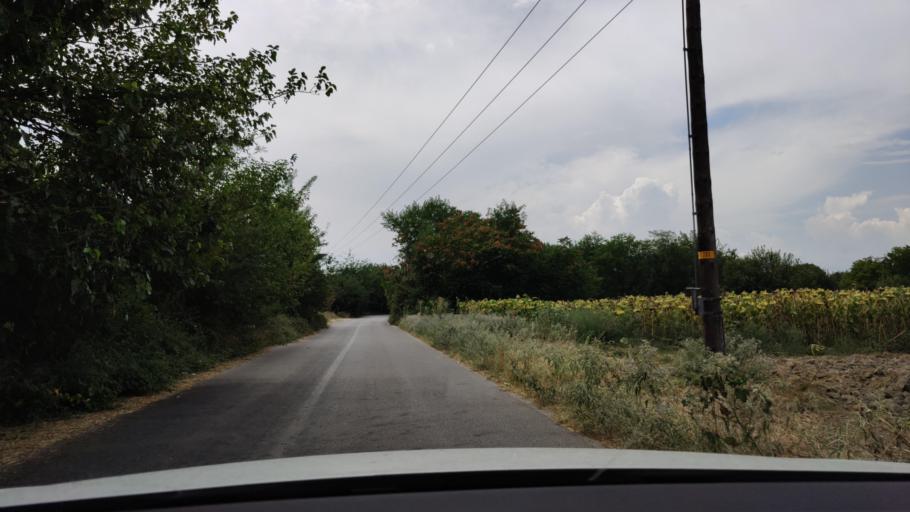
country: GR
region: Central Macedonia
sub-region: Nomos Serron
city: Serres
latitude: 41.0692
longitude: 23.5593
